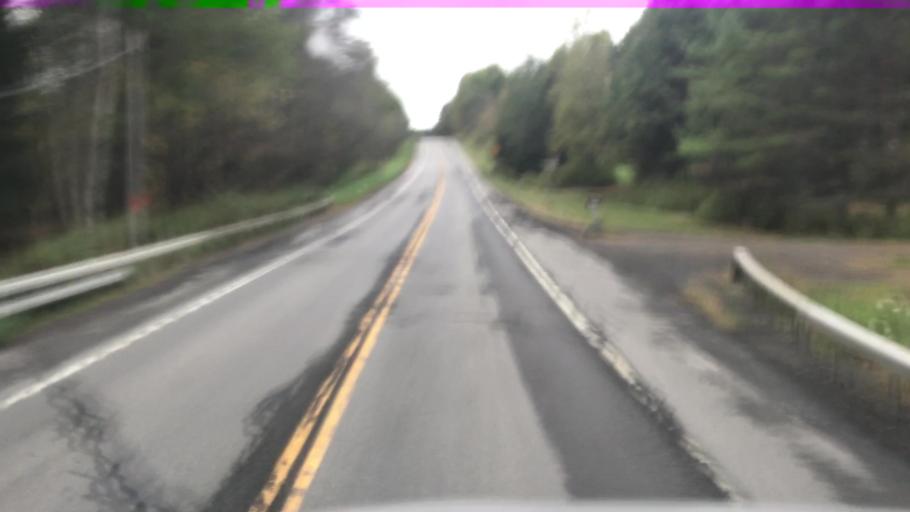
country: US
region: New York
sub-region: Otsego County
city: West End
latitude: 42.5243
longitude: -75.1622
